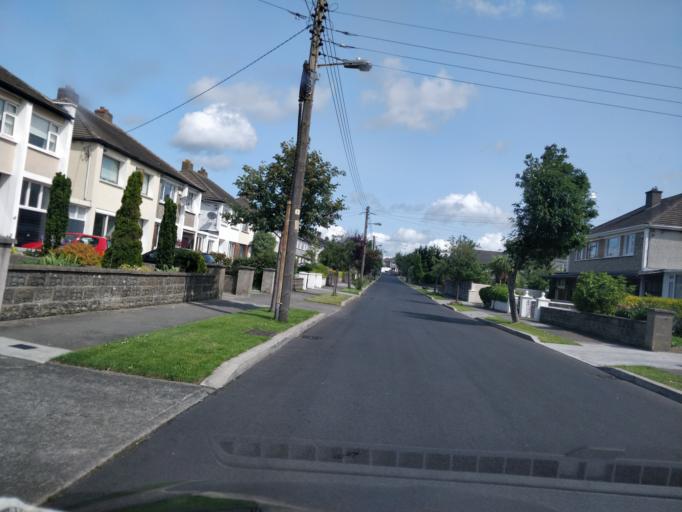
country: IE
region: Leinster
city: Dundrum
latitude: 53.2835
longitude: -6.2543
